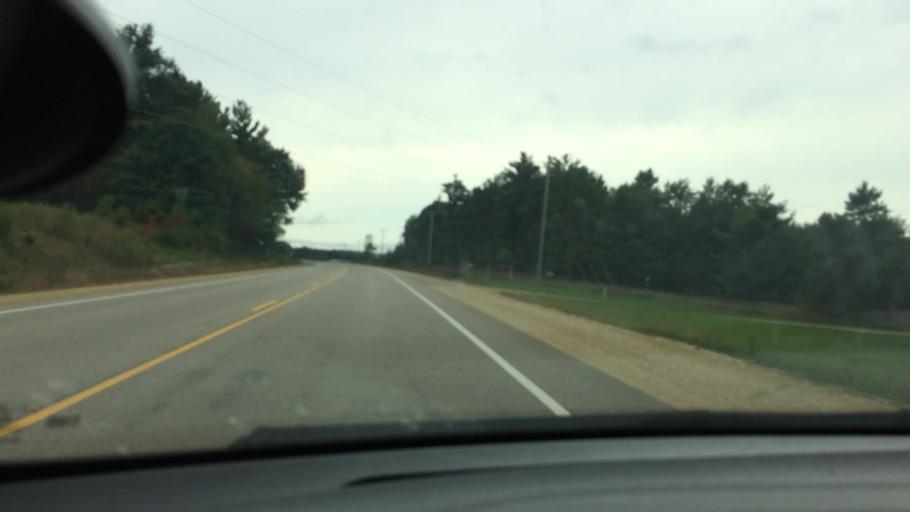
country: US
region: Wisconsin
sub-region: Trempealeau County
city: Osseo
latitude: 44.5900
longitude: -91.1707
